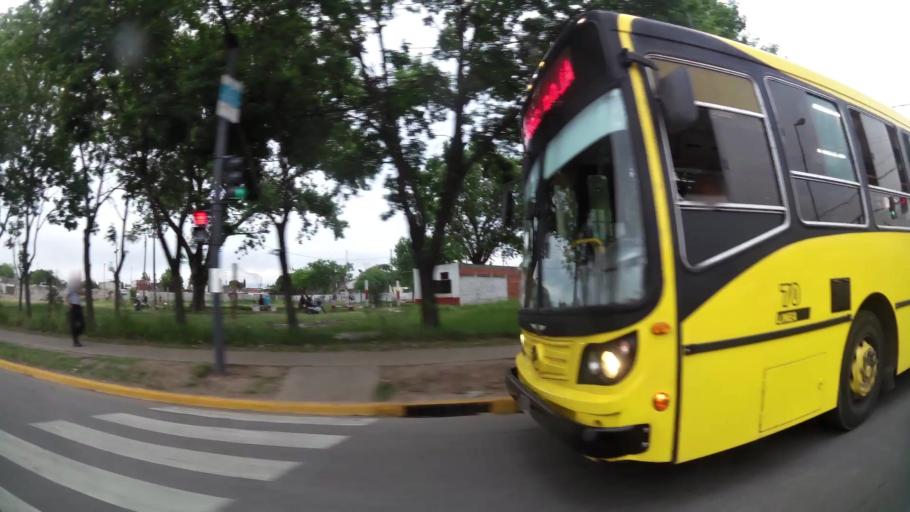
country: AR
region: Santa Fe
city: Granadero Baigorria
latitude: -32.9034
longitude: -60.7009
